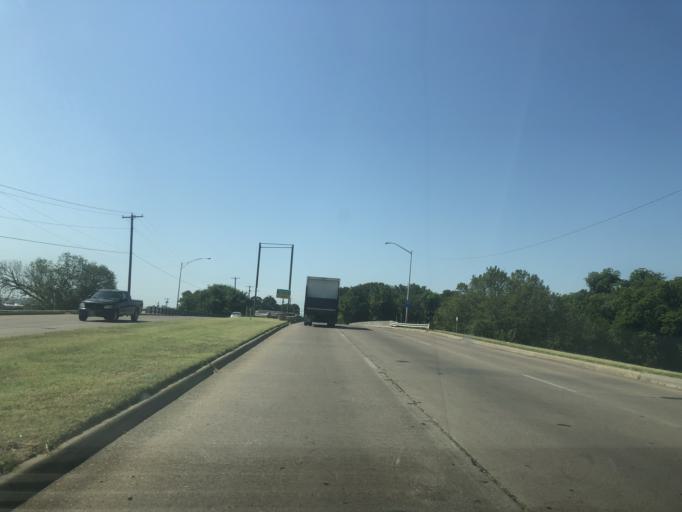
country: US
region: Texas
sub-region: Tarrant County
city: River Oaks
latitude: 32.7651
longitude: -97.3611
